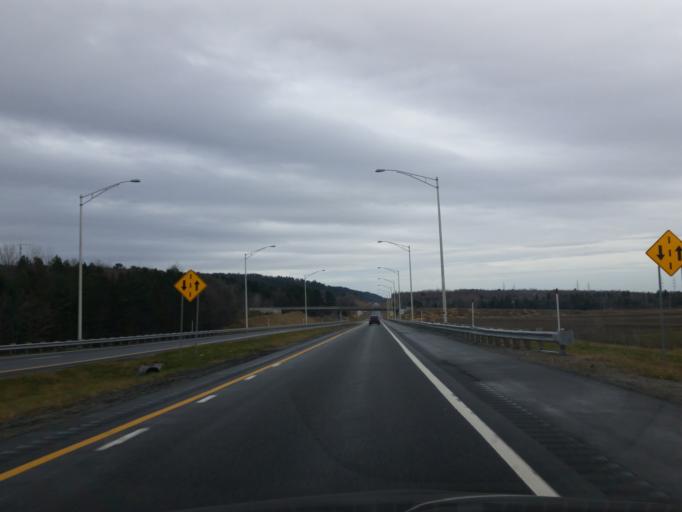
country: CA
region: Quebec
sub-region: Outaouais
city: Papineauville
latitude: 45.6720
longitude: -74.9220
